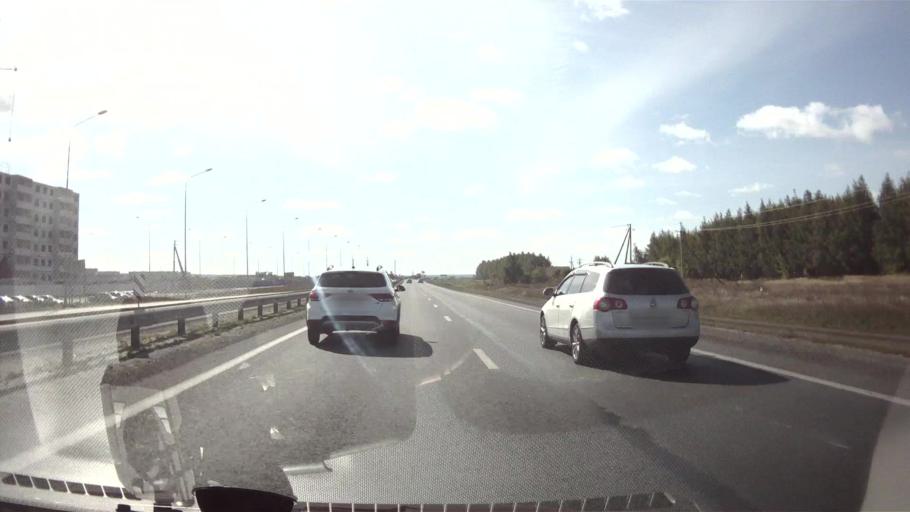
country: RU
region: Ulyanovsk
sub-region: Ulyanovskiy Rayon
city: Ulyanovsk
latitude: 54.2824
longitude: 48.2581
